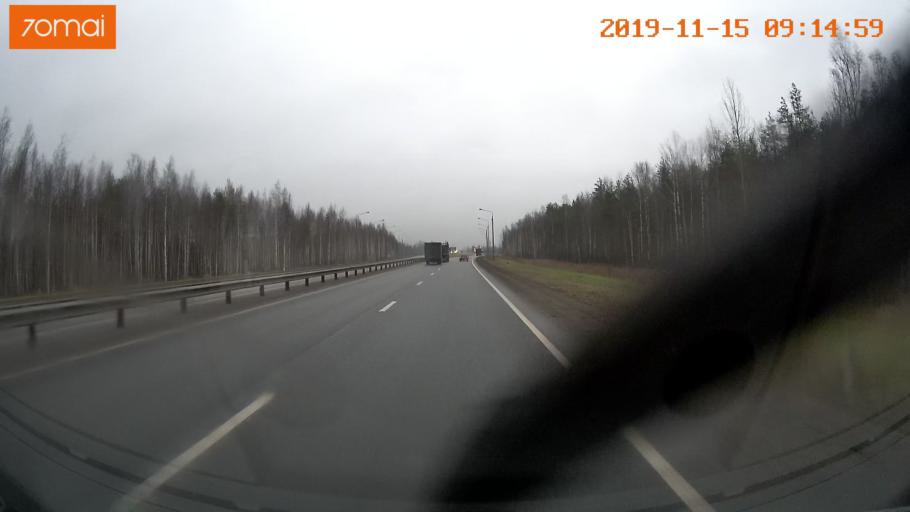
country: RU
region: Vologda
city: Tonshalovo
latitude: 59.2334
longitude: 37.9635
